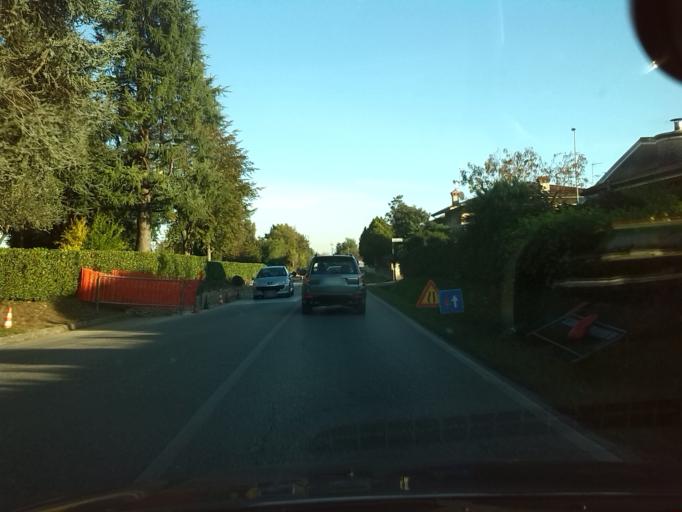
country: IT
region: Friuli Venezia Giulia
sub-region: Provincia di Udine
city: Colugna
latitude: 46.0960
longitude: 13.1855
